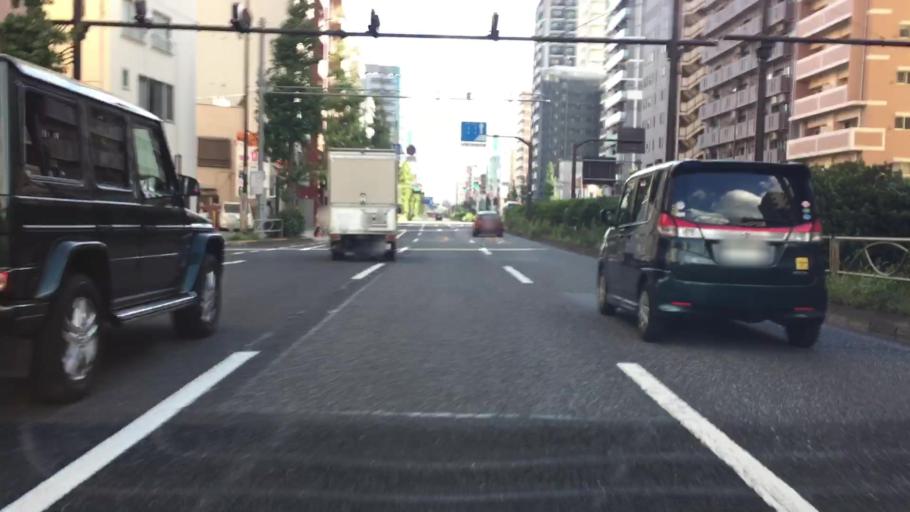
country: JP
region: Saitama
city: Soka
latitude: 35.7544
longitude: 139.8013
